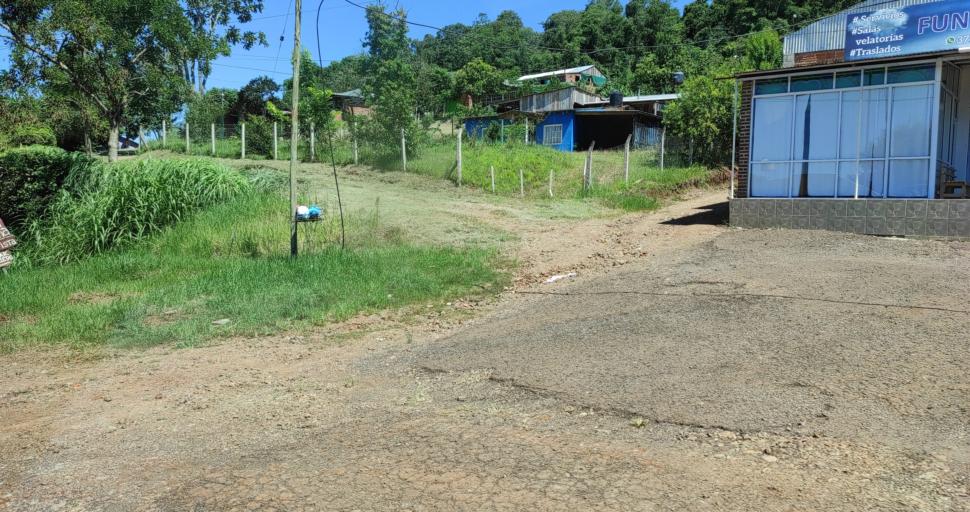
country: AR
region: Misiones
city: El Soberbio
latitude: -27.2889
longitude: -54.2107
